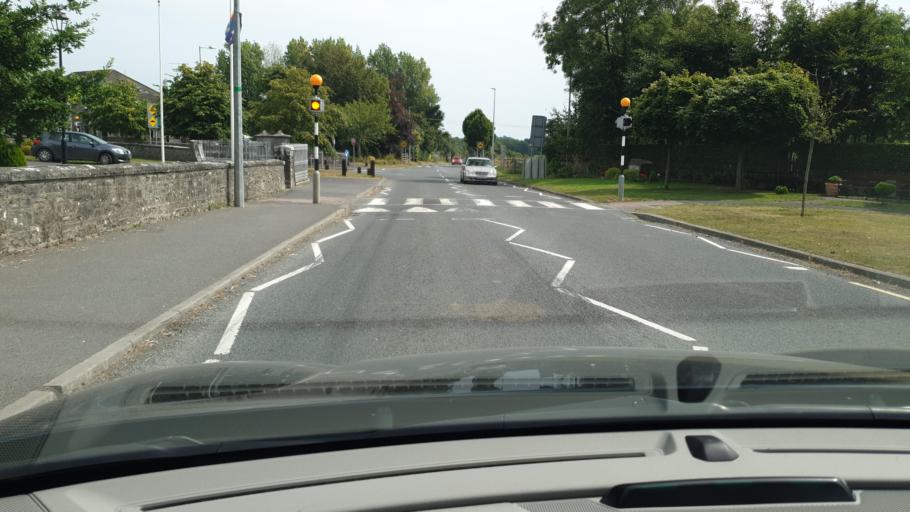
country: IE
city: Kentstown
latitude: 53.6276
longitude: -6.5338
